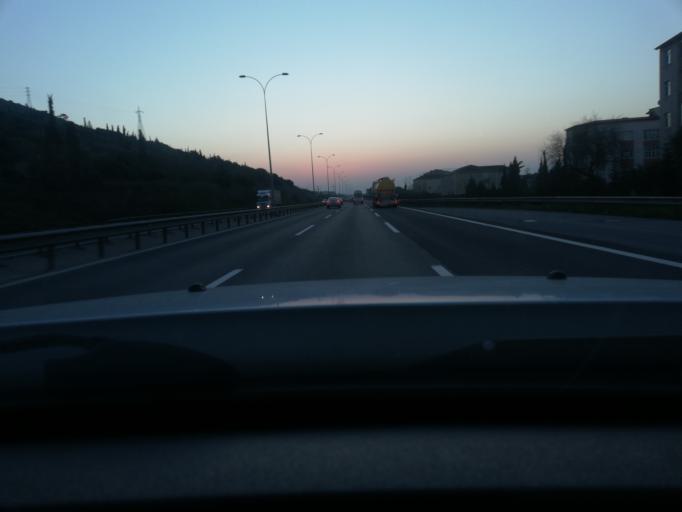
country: TR
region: Kocaeli
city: Korfez
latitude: 40.7772
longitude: 29.7490
